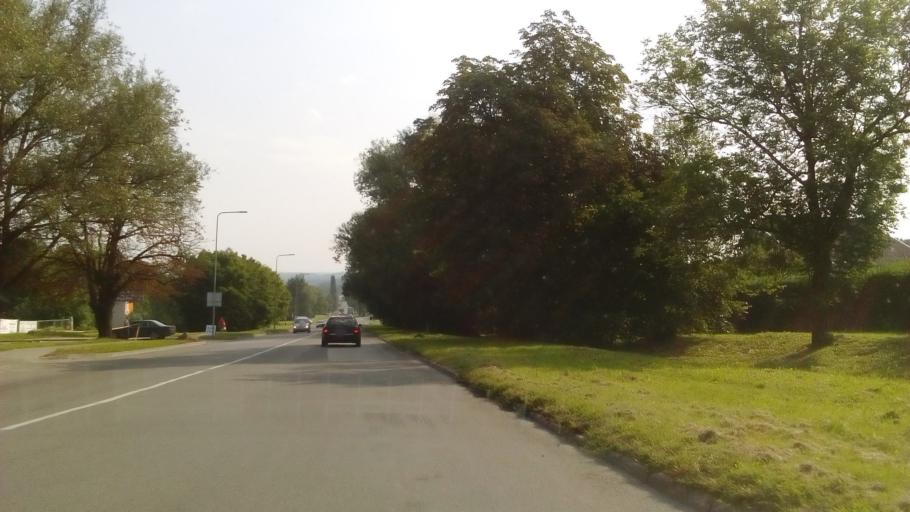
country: LT
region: Alytaus apskritis
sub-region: Alytus
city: Alytus
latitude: 54.3868
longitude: 24.0282
